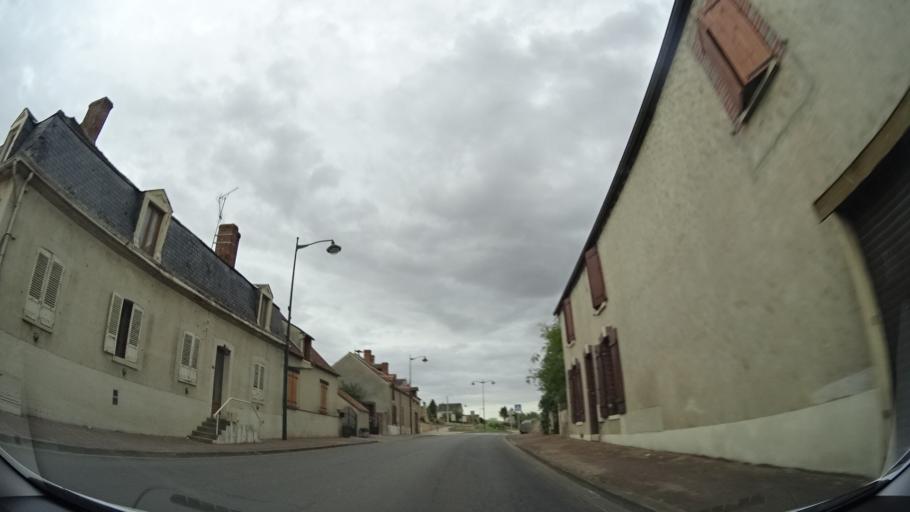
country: FR
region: Centre
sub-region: Departement du Loiret
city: Saint-Germain-des-Pres
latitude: 47.9537
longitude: 2.8488
